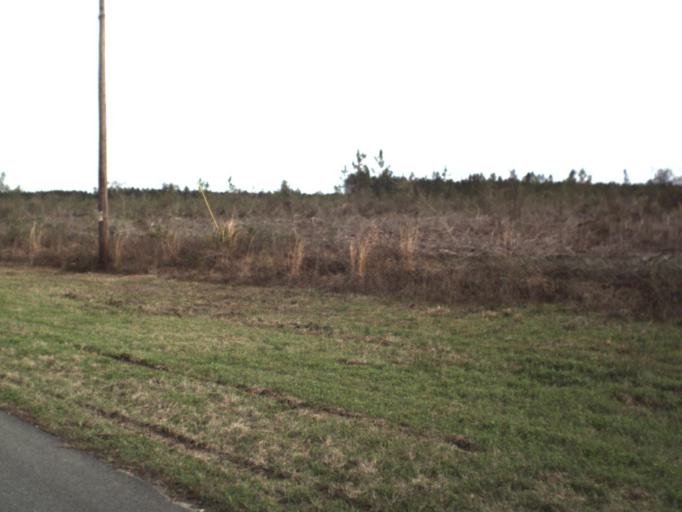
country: US
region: Florida
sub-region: Bay County
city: Callaway
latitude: 30.1481
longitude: -85.4589
